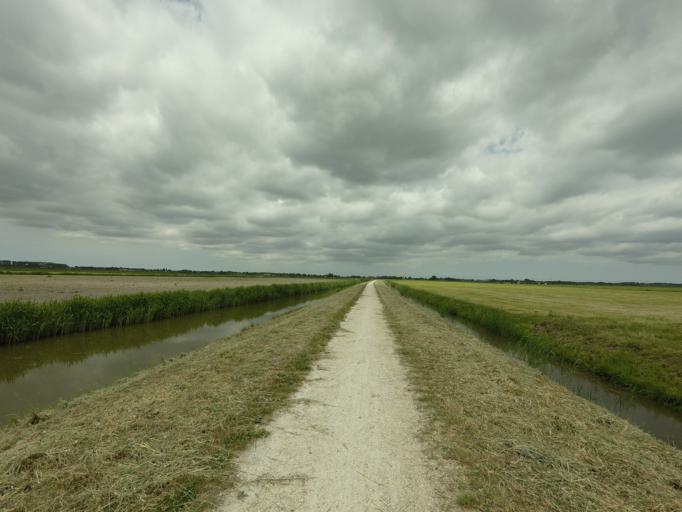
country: NL
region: North Holland
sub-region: Gemeente Beemster
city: Halfweg
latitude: 52.6022
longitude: 4.9733
